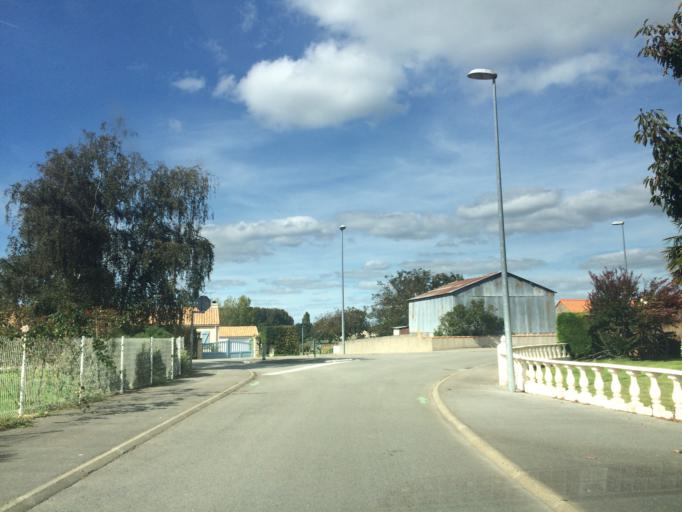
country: FR
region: Pays de la Loire
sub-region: Departement de la Loire-Atlantique
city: Chemere
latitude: 47.1224
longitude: -1.9189
